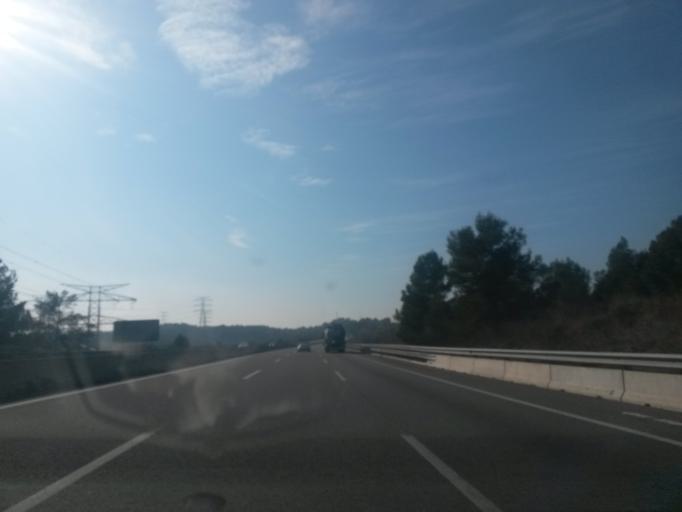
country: ES
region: Catalonia
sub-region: Provincia de Girona
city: Viladasens
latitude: 42.1046
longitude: 2.9081
